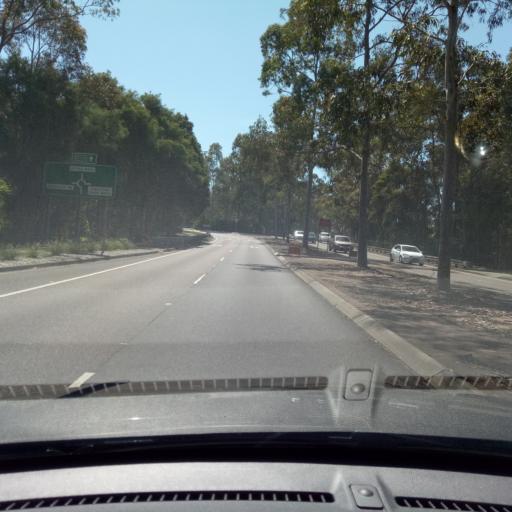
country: AU
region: New South Wales
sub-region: Wyong Shire
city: Chittaway Bay
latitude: -33.3370
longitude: 151.4304
